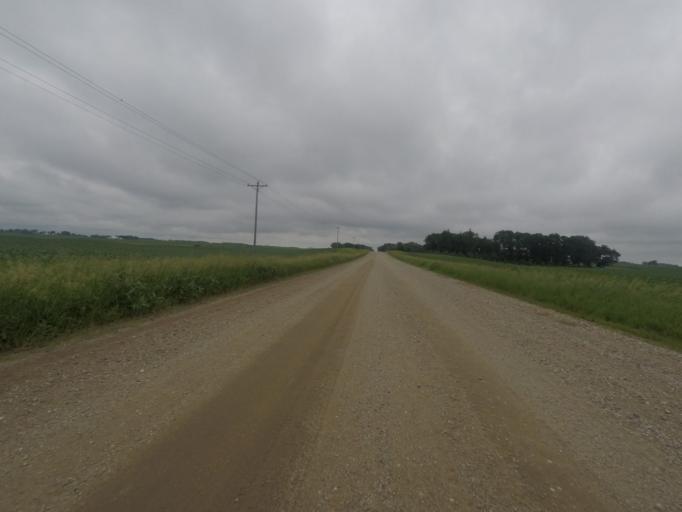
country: US
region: Minnesota
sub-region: Steele County
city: Owatonna
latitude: 44.0373
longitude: -93.1044
